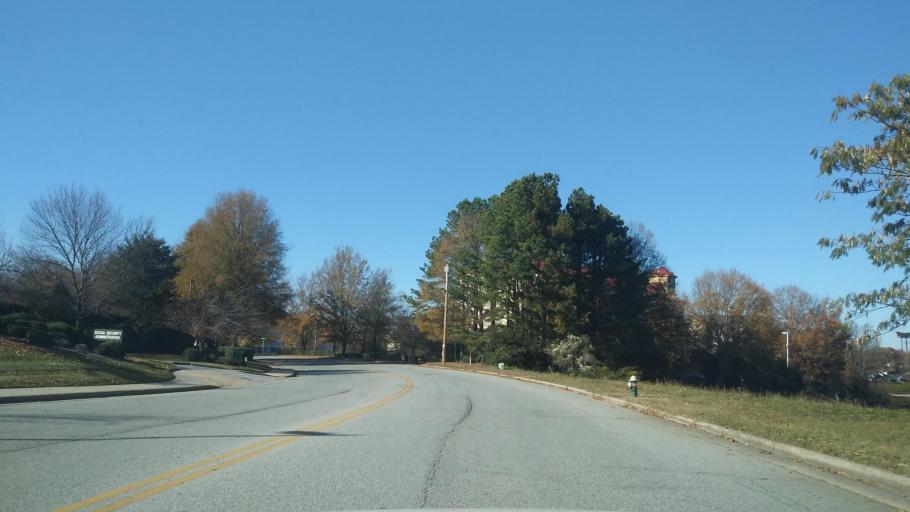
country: US
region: North Carolina
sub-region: Guilford County
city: Jamestown
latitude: 36.0523
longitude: -79.8924
